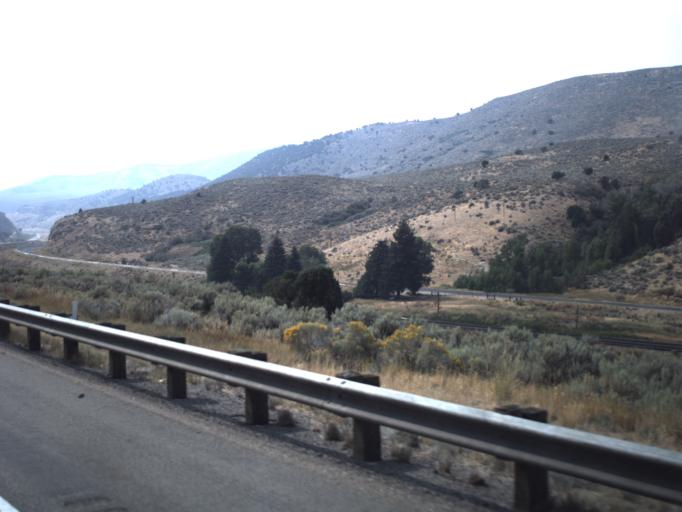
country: US
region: Utah
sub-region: Summit County
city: Coalville
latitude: 41.0491
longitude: -111.3007
